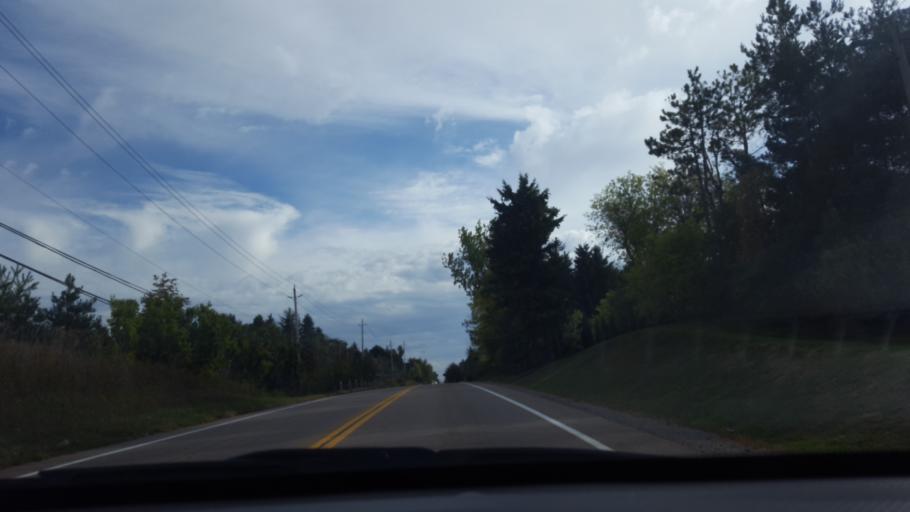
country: CA
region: Ontario
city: Vaughan
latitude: 43.9184
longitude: -79.5530
